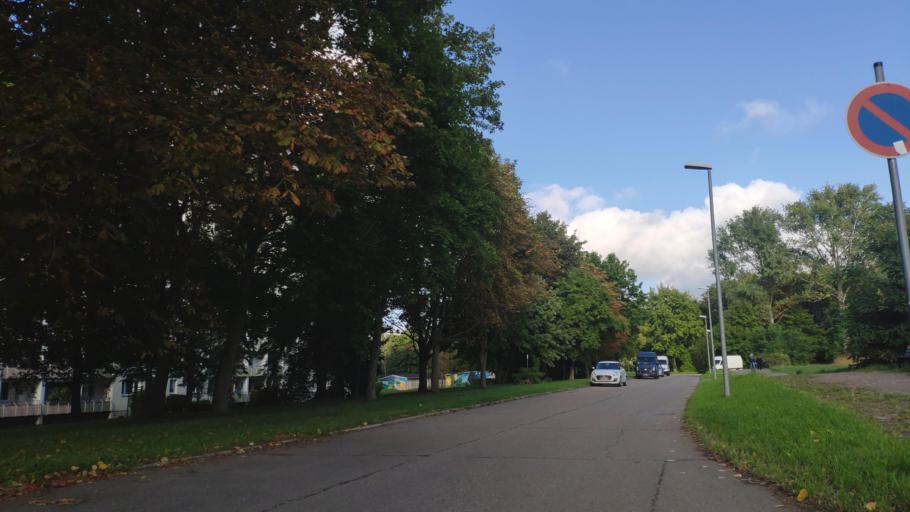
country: DE
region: Saxony
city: Hilbersdorf
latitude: 50.8239
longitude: 12.9605
